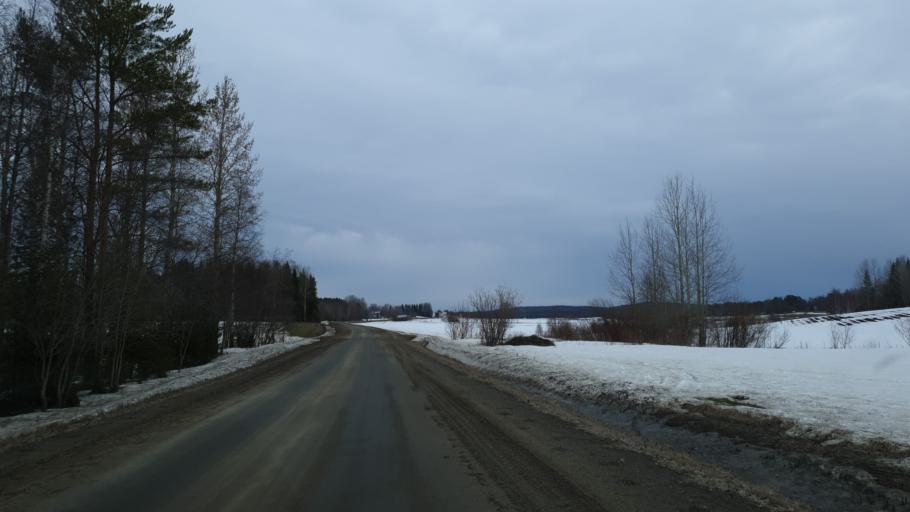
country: SE
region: Vaesterbotten
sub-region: Skelleftea Kommun
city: Burea
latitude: 64.3250
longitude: 21.1386
